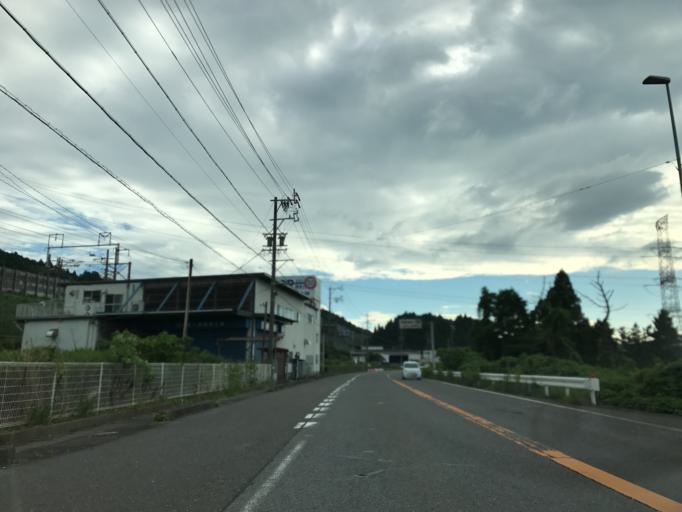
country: JP
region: Gifu
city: Tarui
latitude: 35.3669
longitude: 136.4931
